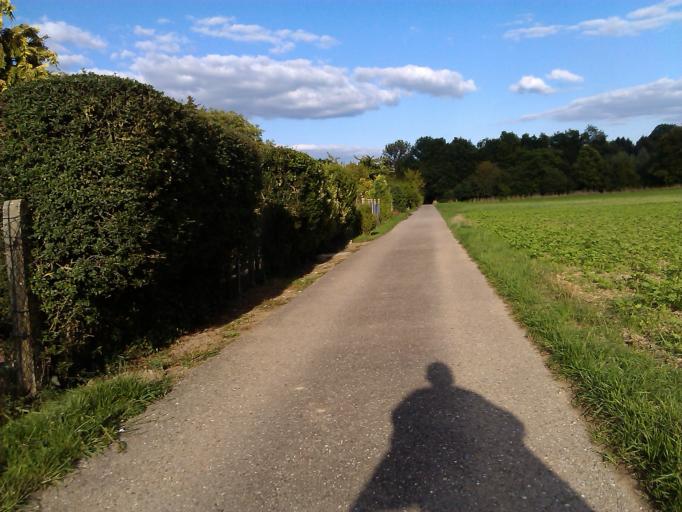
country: DE
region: Baden-Wuerttemberg
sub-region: Regierungsbezirk Stuttgart
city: Flein
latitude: 49.1237
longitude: 9.1905
